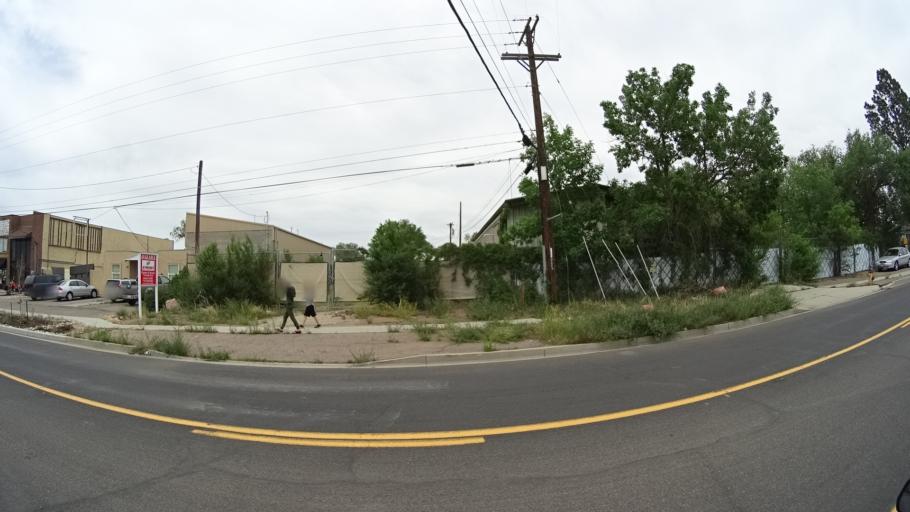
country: US
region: Colorado
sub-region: El Paso County
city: Colorado Springs
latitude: 38.8388
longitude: -104.7846
